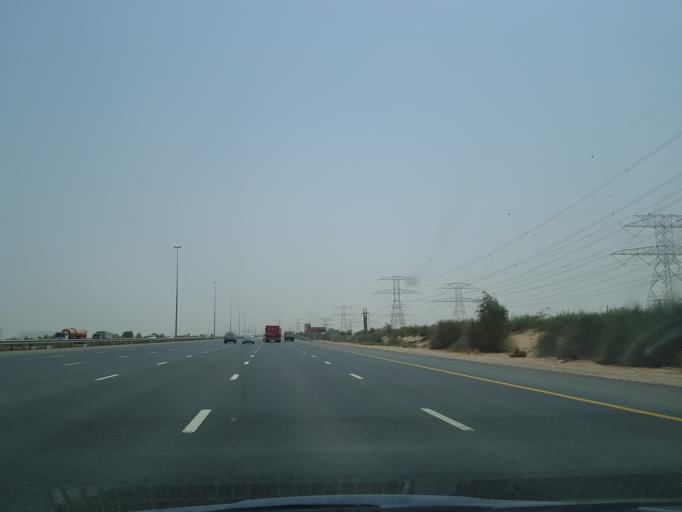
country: AE
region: Dubai
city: Dubai
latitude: 25.0652
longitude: 55.3393
